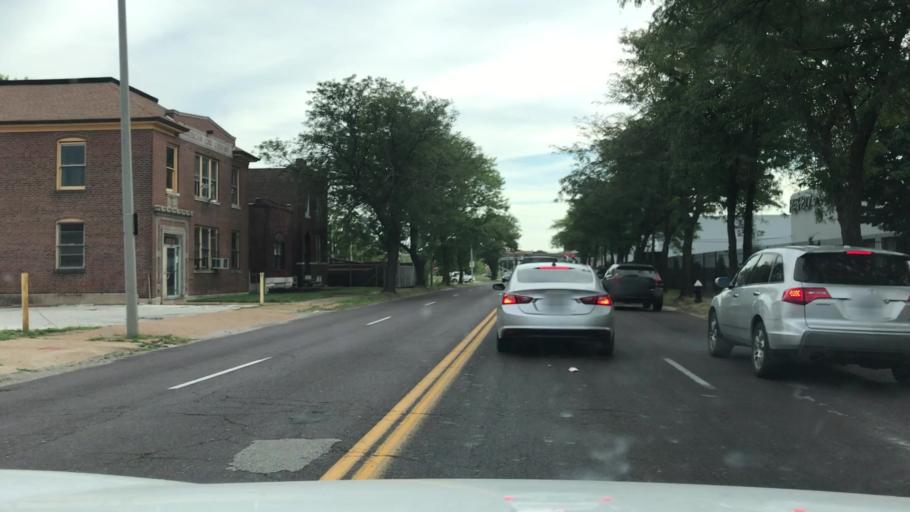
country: US
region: Missouri
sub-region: City of Saint Louis
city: St. Louis
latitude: 38.6208
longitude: -90.2574
